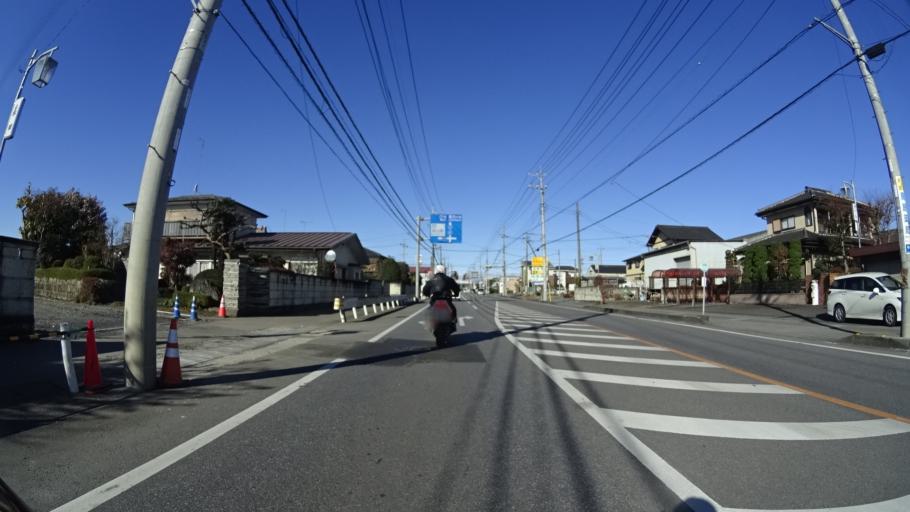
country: JP
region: Tochigi
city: Kanuma
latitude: 36.5318
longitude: 139.7475
